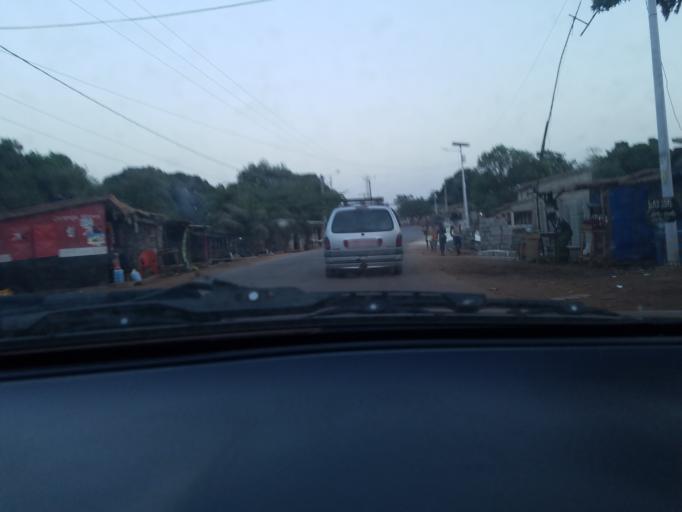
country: GN
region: Kindia
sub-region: Prefecture de Dubreka
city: Dubreka
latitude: 9.7892
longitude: -13.4890
